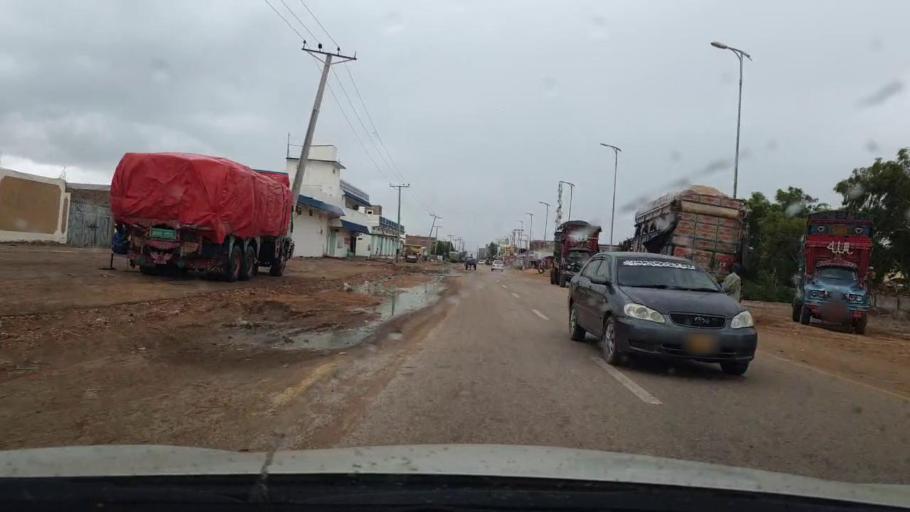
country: PK
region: Sindh
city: Kario
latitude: 24.6532
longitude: 68.5276
